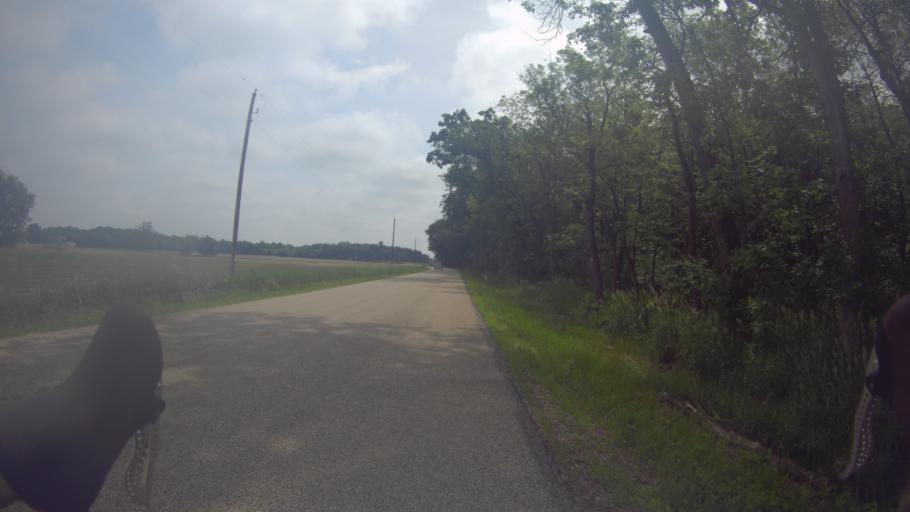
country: US
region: Wisconsin
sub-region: Jefferson County
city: Cambridge
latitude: 42.9234
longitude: -89.0169
